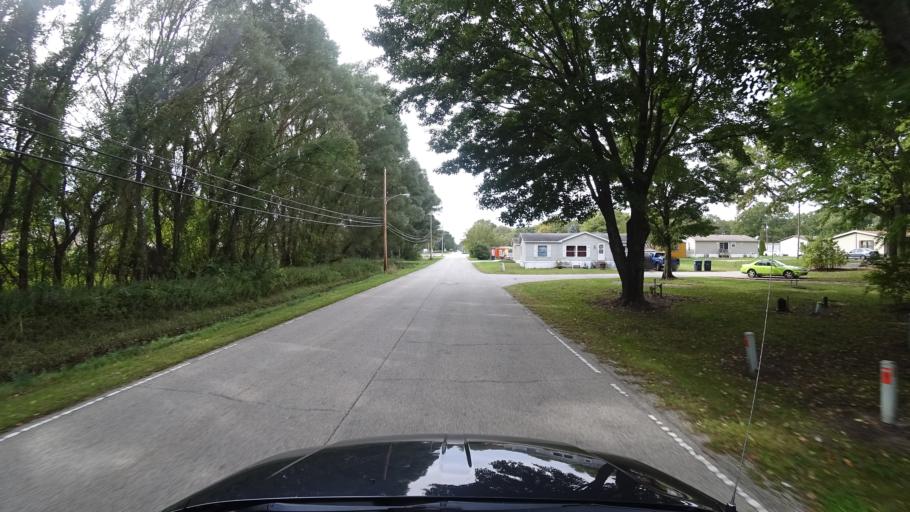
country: US
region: Indiana
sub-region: LaPorte County
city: Long Beach
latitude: 41.7382
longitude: -86.8243
